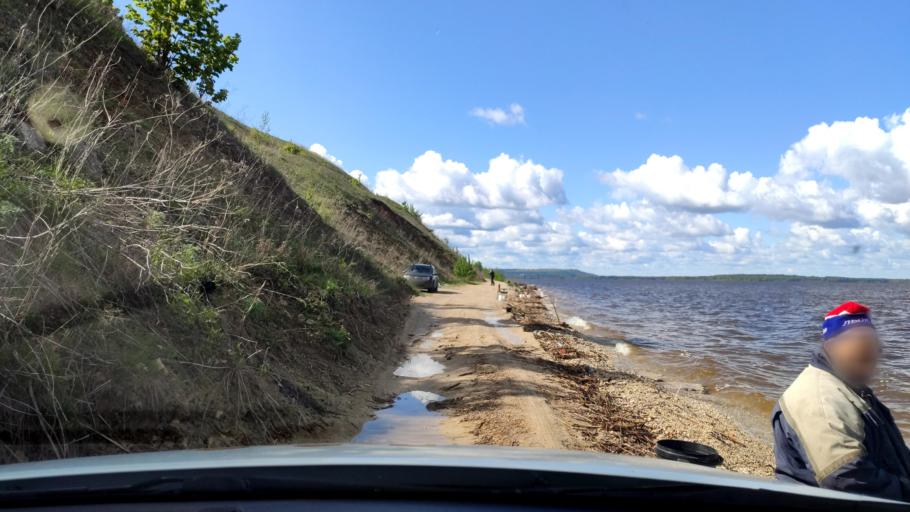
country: RU
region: Tatarstan
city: Sviyazhsk
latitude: 55.7779
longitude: 48.6929
